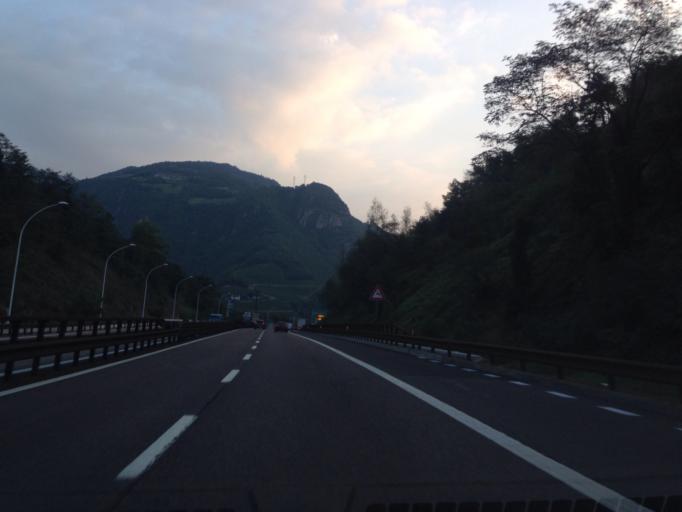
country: IT
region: Trentino-Alto Adige
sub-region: Bolzano
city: Fie Allo Sciliar
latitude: 46.5287
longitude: 11.4904
